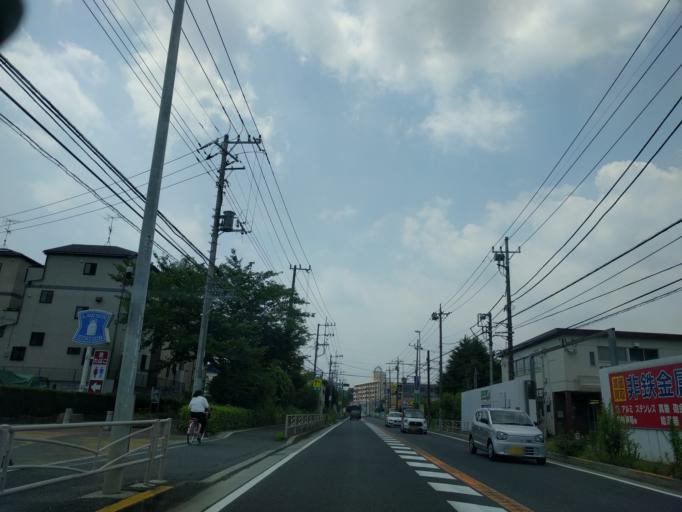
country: JP
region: Kanagawa
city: Minami-rinkan
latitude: 35.4916
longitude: 139.5131
